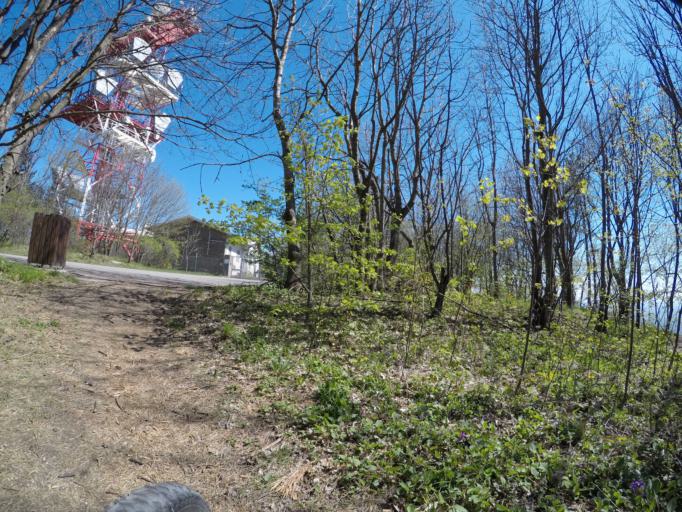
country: AT
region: Lower Austria
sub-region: Politischer Bezirk Modling
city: Gumpoldskirchen
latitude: 48.0523
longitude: 16.2520
